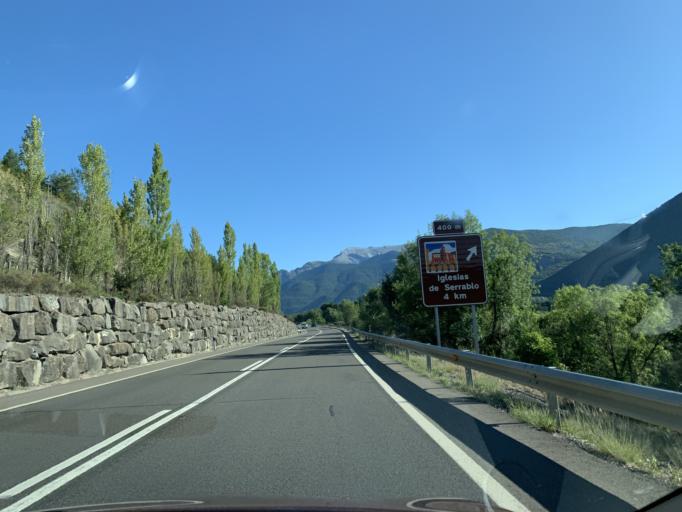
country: ES
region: Aragon
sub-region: Provincia de Huesca
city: Biescas
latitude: 42.5735
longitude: -0.3248
